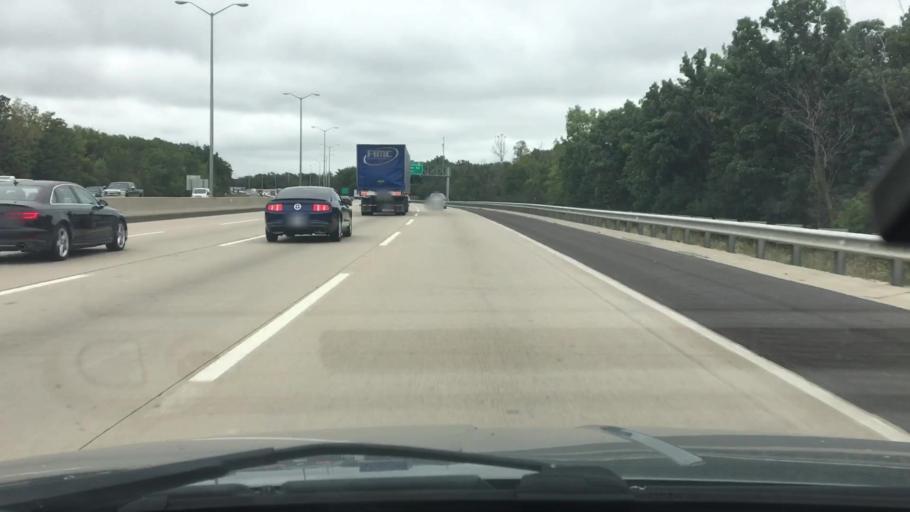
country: US
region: Illinois
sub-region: Lake County
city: Riverwoods
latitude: 42.1233
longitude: -87.8839
